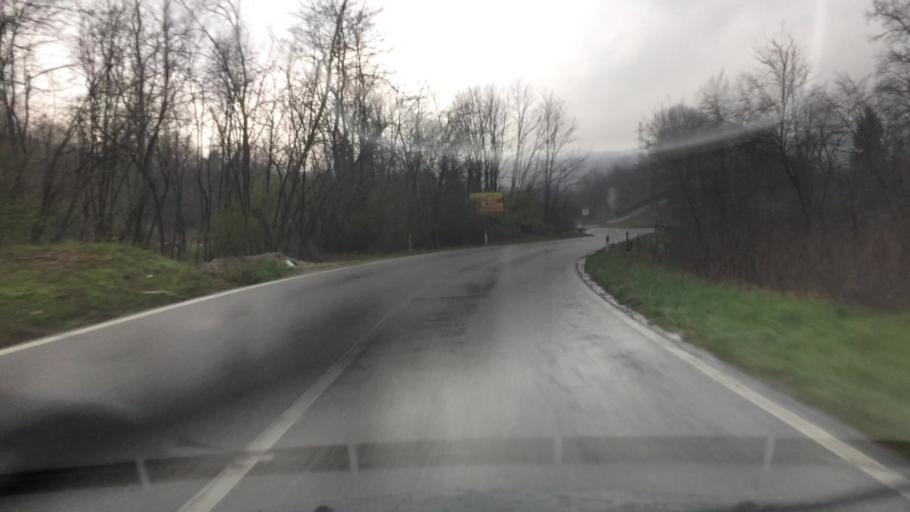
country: IT
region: Lombardy
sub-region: Provincia di Como
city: Montesolaro
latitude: 45.7240
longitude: 9.1056
